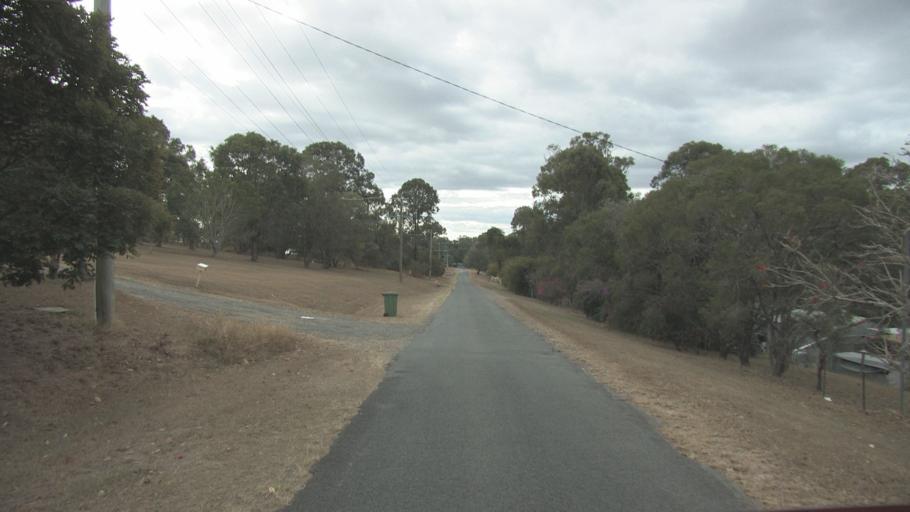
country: AU
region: Queensland
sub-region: Logan
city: Cedar Vale
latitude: -27.8823
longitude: 153.0205
